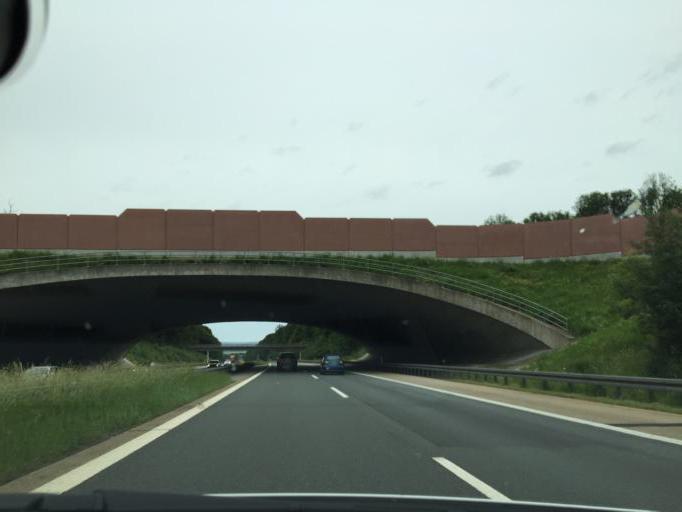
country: DE
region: Bavaria
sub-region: Regierungsbezirk Unterfranken
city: Oberthulba
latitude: 50.2173
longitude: 9.9083
